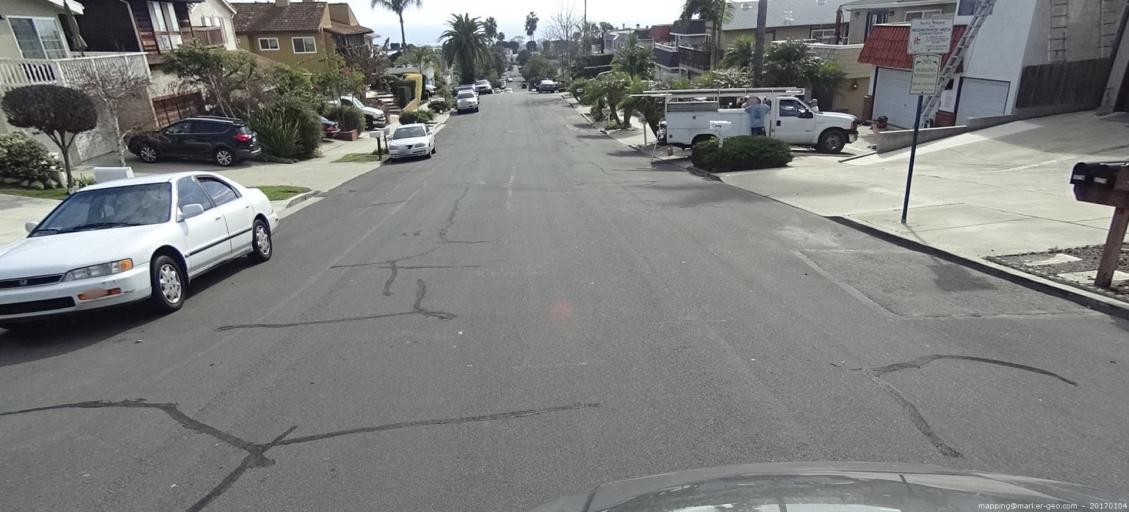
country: US
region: California
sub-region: Orange County
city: Dana Point
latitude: 33.4724
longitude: -117.6947
